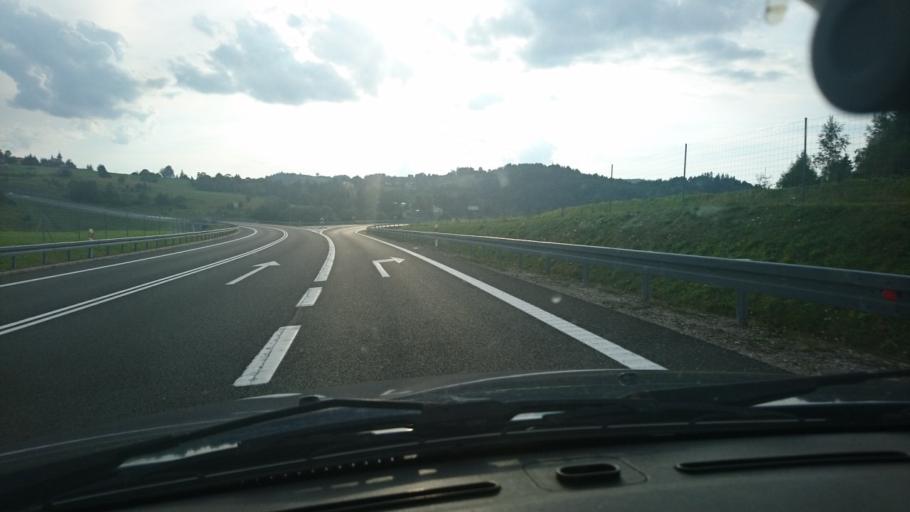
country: PL
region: Silesian Voivodeship
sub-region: Powiat zywiecki
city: Kamesznica
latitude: 49.5485
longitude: 19.0268
